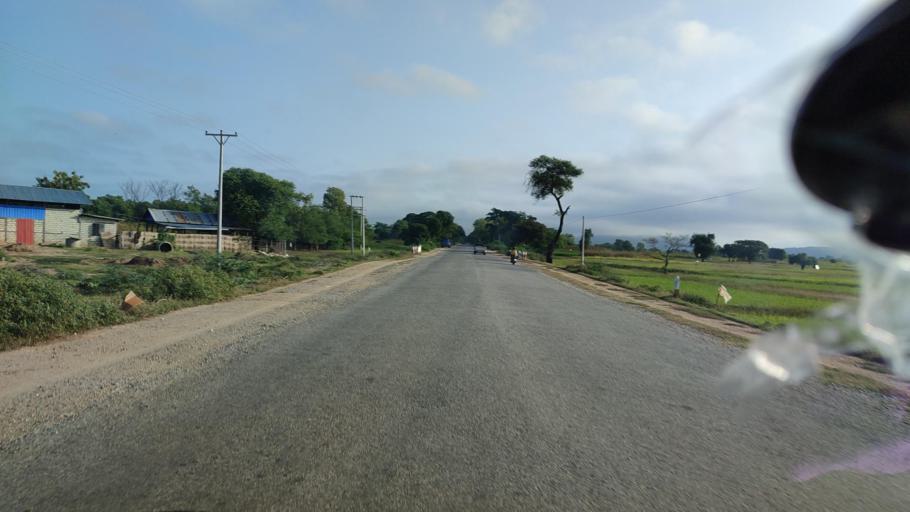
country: MM
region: Mandalay
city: Yamethin
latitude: 20.6908
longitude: 96.1612
